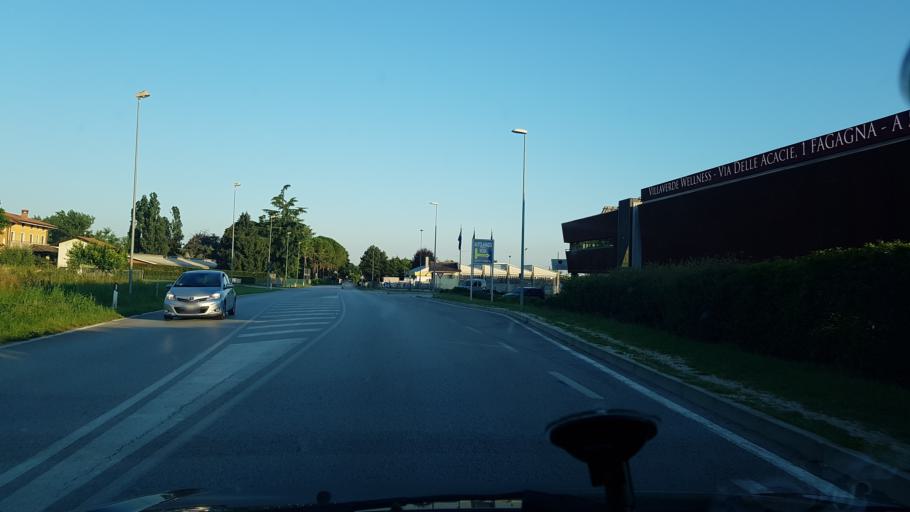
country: IT
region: Friuli Venezia Giulia
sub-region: Provincia di Udine
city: Fagagna
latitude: 46.1038
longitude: 13.0941
